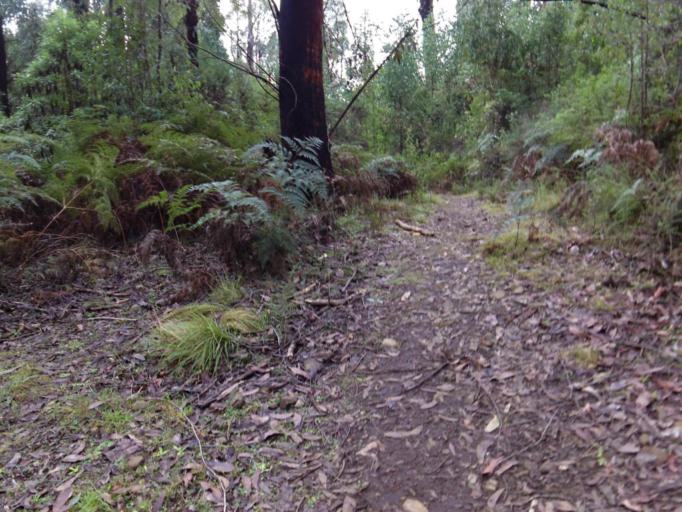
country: AU
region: Victoria
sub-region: Yarra Ranges
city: Millgrove
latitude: -37.5315
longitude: 145.7519
